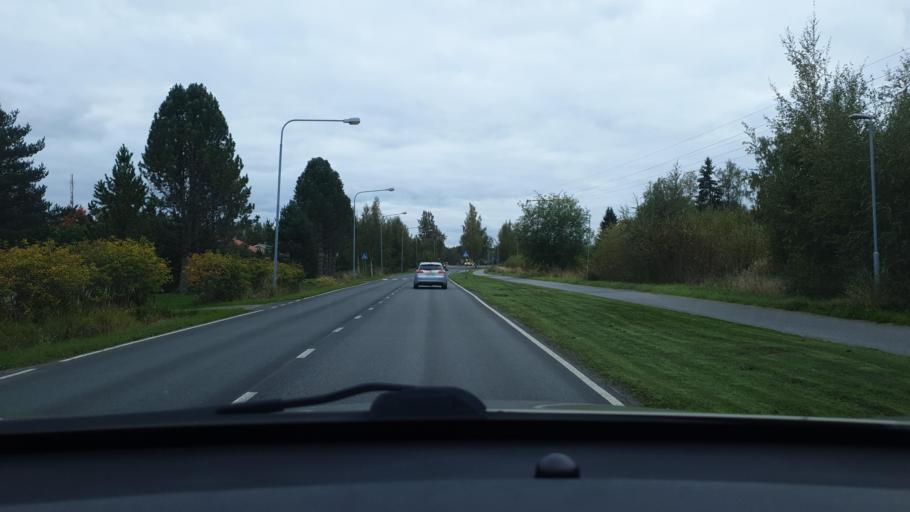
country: FI
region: Ostrobothnia
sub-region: Vaasa
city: Teeriniemi
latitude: 63.0919
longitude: 21.6986
